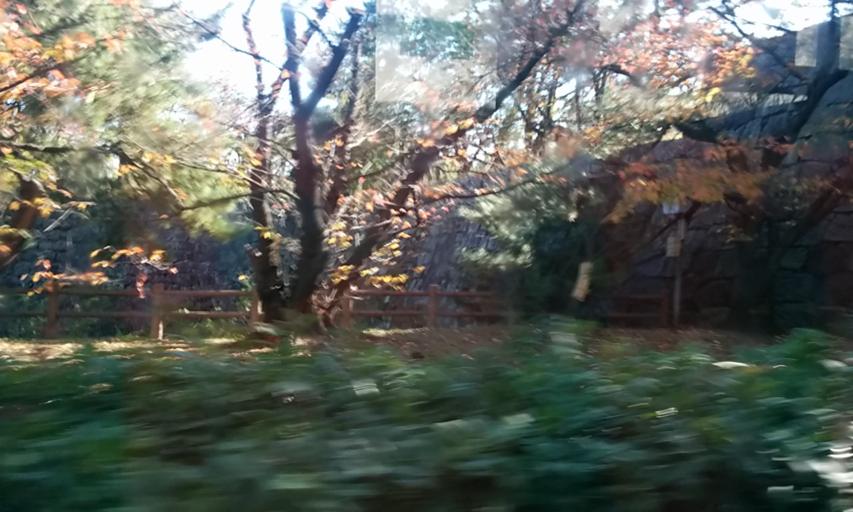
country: JP
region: Wakayama
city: Wakayama-shi
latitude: 34.2287
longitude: 135.1689
